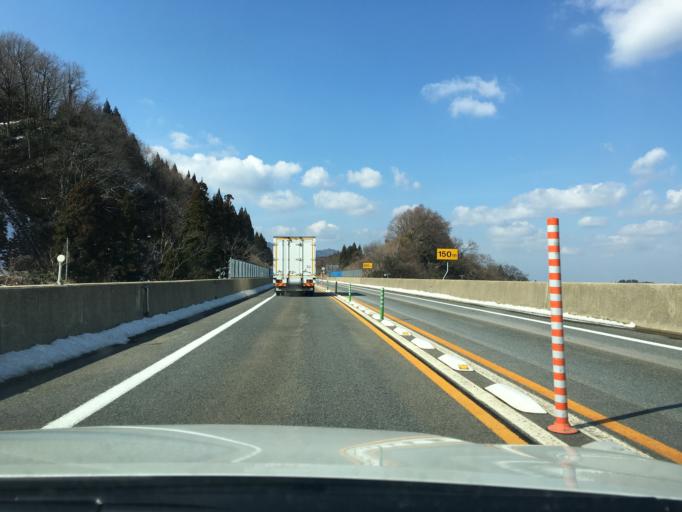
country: JP
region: Yamagata
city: Tsuruoka
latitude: 38.6228
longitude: 139.8423
